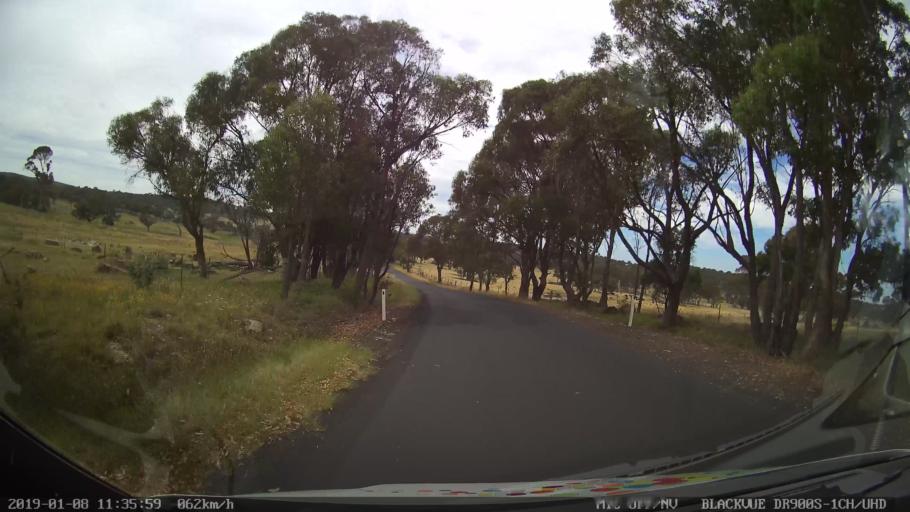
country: AU
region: New South Wales
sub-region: Guyra
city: Guyra
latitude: -30.3424
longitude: 151.5399
